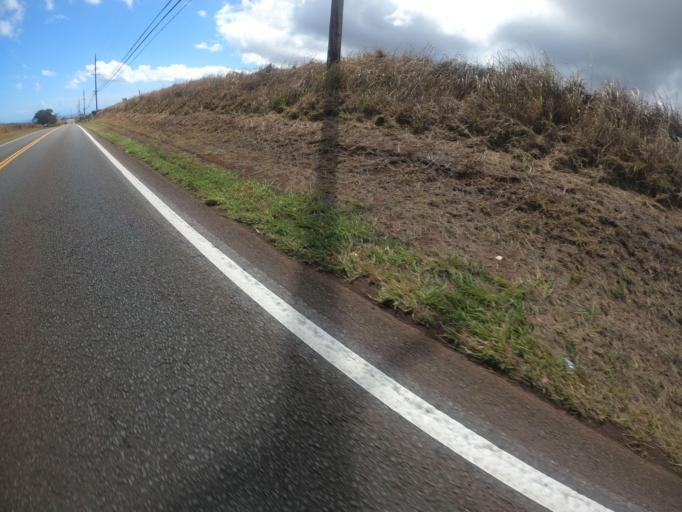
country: US
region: Hawaii
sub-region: Honolulu County
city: Village Park
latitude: 21.4315
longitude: -158.0568
